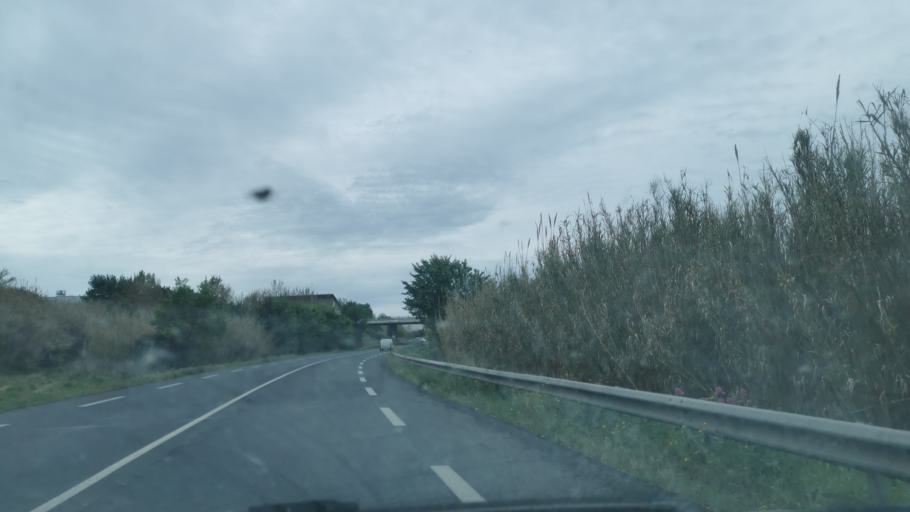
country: FR
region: Languedoc-Roussillon
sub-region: Departement de l'Herault
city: Gigean
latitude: 43.4932
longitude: 3.7007
